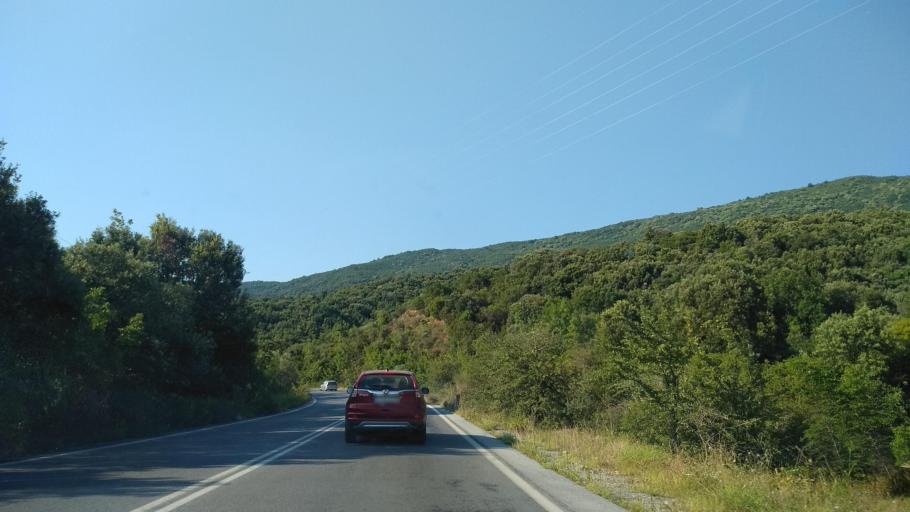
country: GR
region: Central Macedonia
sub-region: Nomos Thessalonikis
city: Stavros
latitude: 40.6432
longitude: 23.7473
